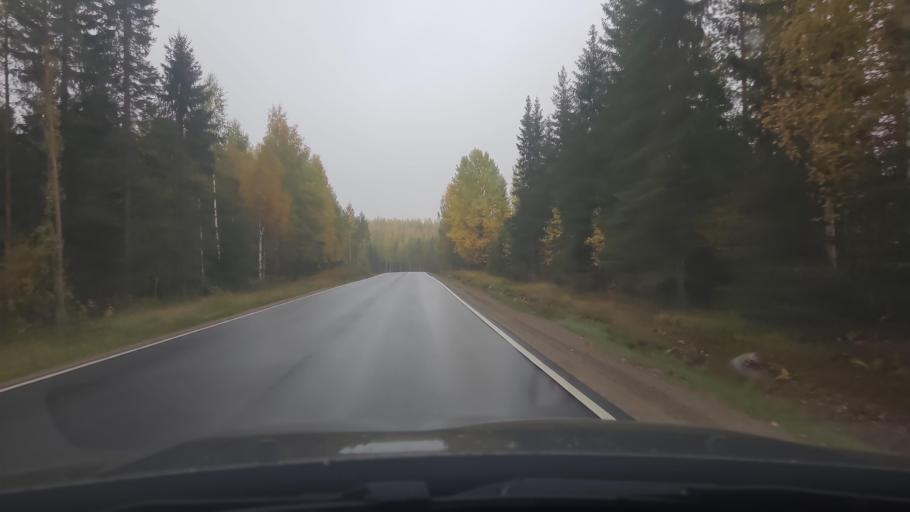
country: FI
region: Northern Savo
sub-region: Varkaus
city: Kangaslampi
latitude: 62.4564
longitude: 28.2710
